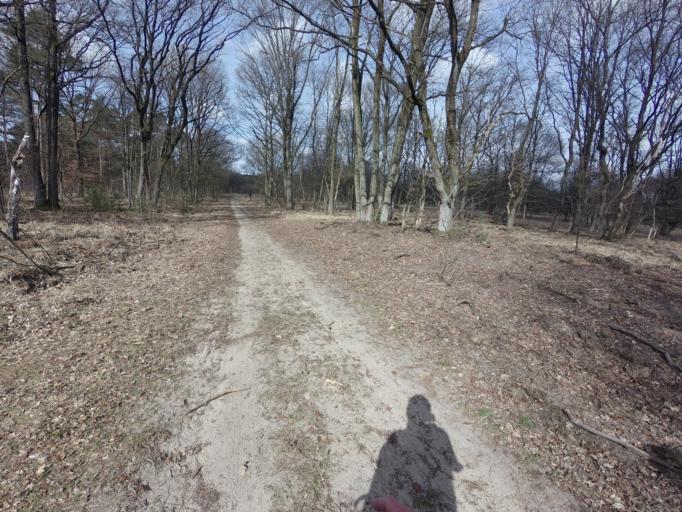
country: NL
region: Limburg
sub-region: Gemeente Roerdalen
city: Vlodrop
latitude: 51.1605
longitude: 6.1283
